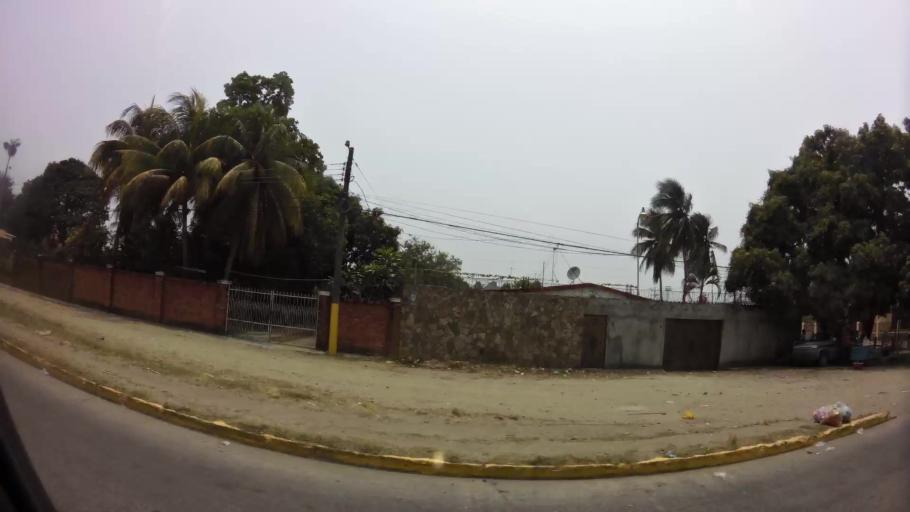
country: HN
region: Yoro
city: El Progreso
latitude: 15.3998
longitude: -87.8134
